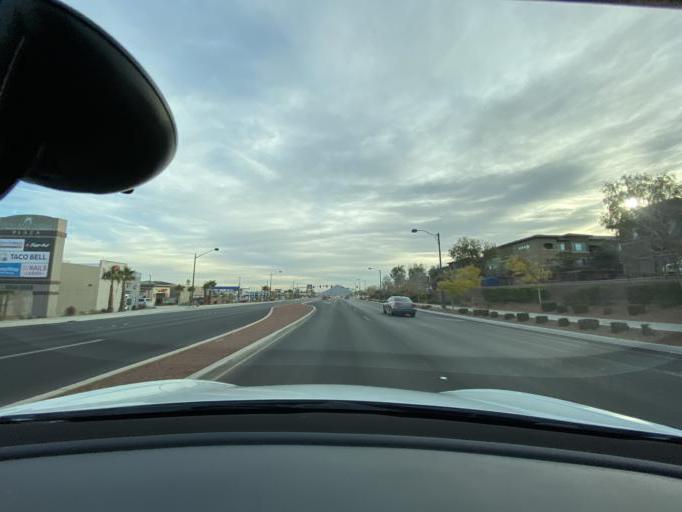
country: US
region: Nevada
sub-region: Clark County
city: Summerlin South
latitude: 36.2861
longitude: -115.3150
